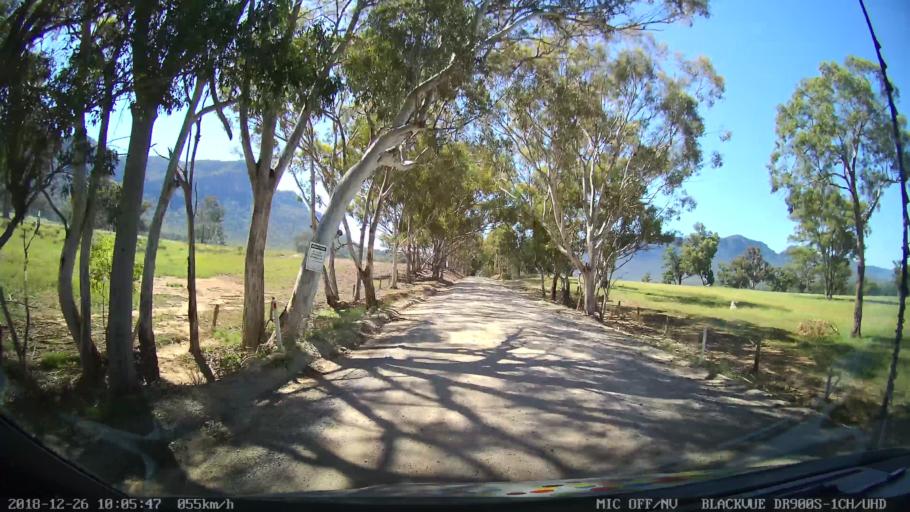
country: AU
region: New South Wales
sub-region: Mid-Western Regional
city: Kandos
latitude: -33.0805
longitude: 150.2142
